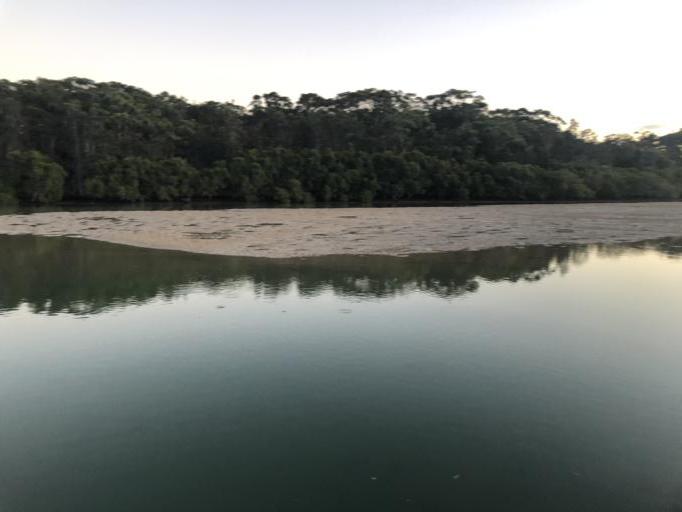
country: AU
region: New South Wales
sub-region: Coffs Harbour
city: Coffs Harbour
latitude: -30.2995
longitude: 153.1332
